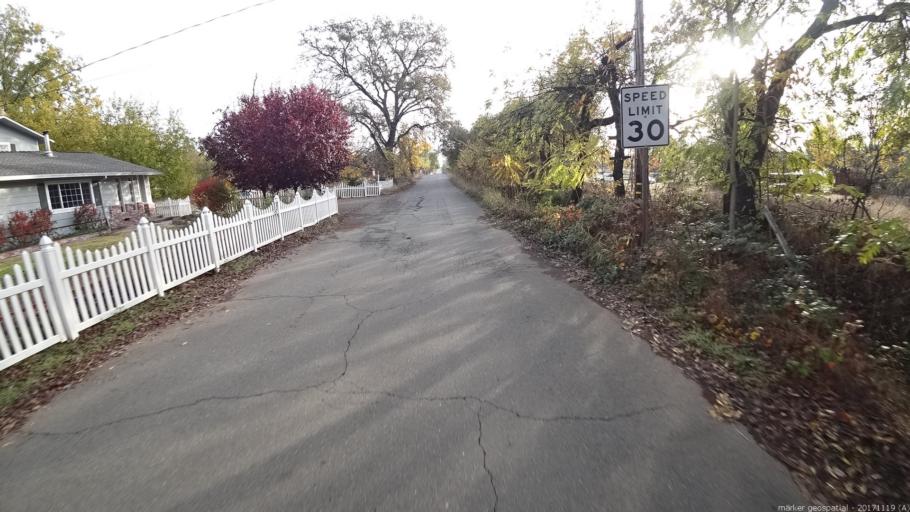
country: US
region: California
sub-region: Shasta County
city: Anderson
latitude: 40.5056
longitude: -122.3462
